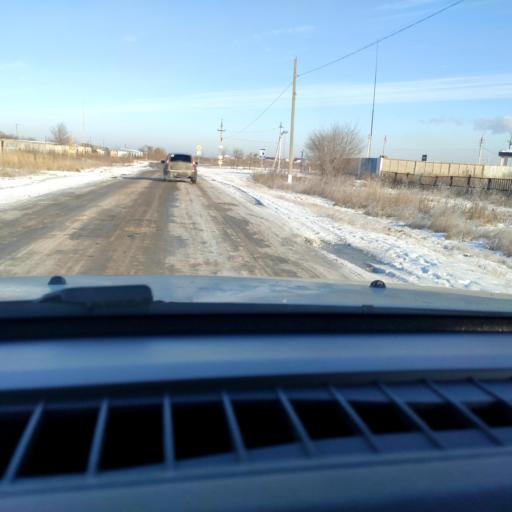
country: RU
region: Samara
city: Podstepki
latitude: 53.5219
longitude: 49.1458
